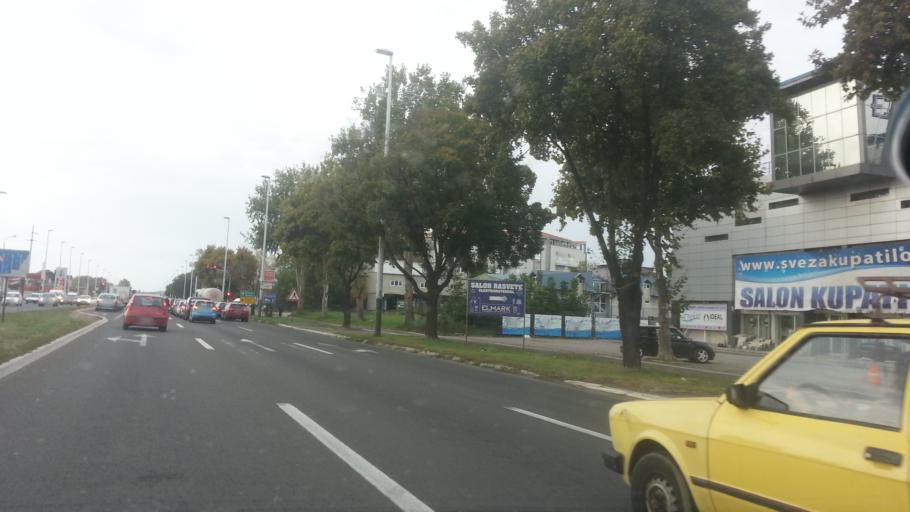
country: RS
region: Central Serbia
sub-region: Belgrade
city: Zemun
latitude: 44.8489
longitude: 20.3729
